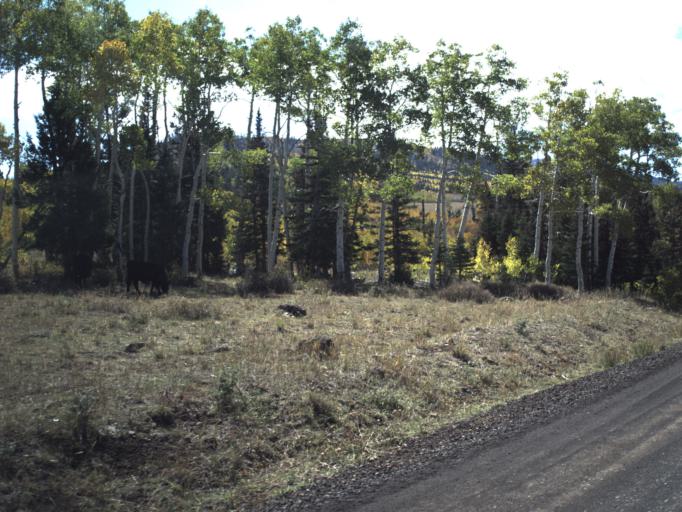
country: US
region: Utah
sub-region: Piute County
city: Junction
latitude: 38.2544
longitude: -112.3327
